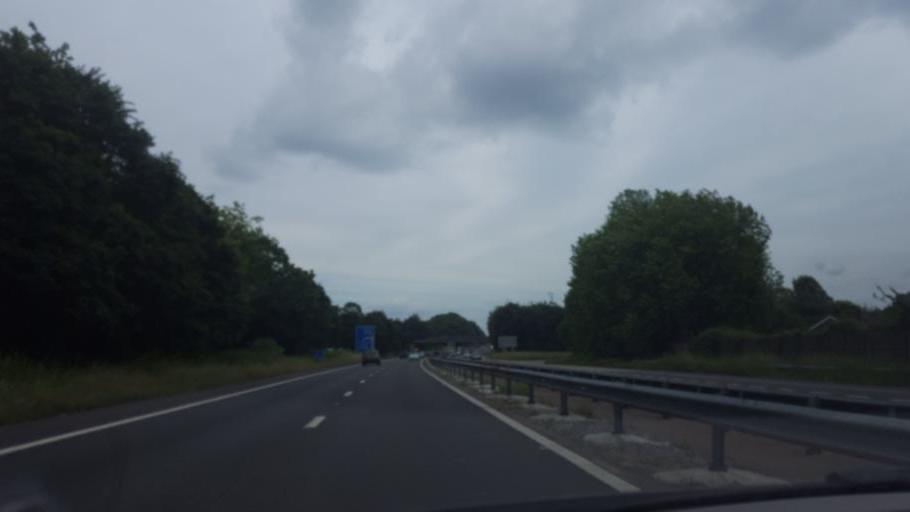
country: GB
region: England
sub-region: Royal Borough of Windsor and Maidenhead
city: Maidenhead
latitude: 51.5089
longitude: -0.7399
